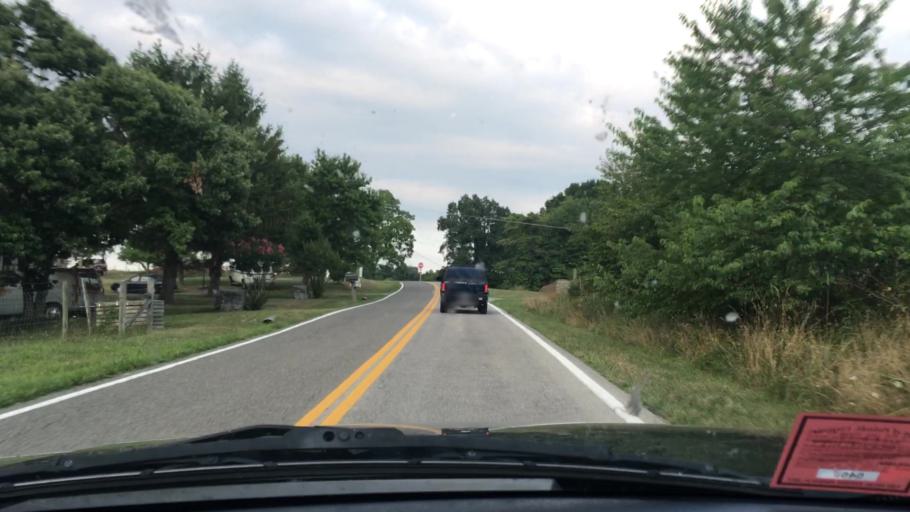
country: US
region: Virginia
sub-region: Pulaski County
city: Dublin
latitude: 37.0565
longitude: -80.6994
